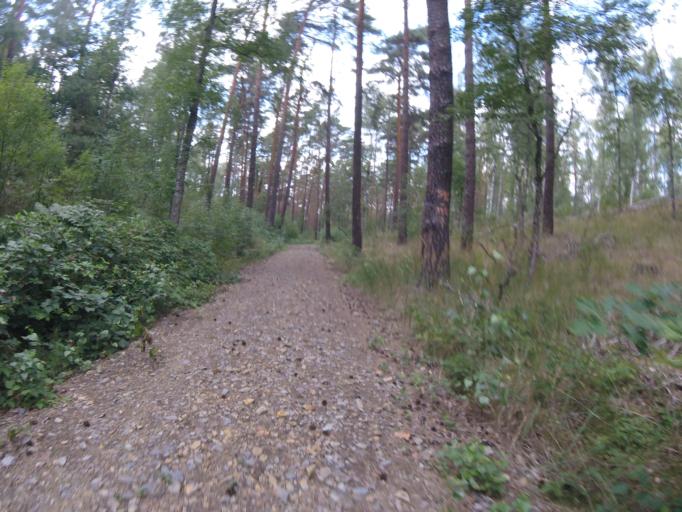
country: DE
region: Brandenburg
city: Schlepzig
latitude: 52.0595
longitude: 13.8016
